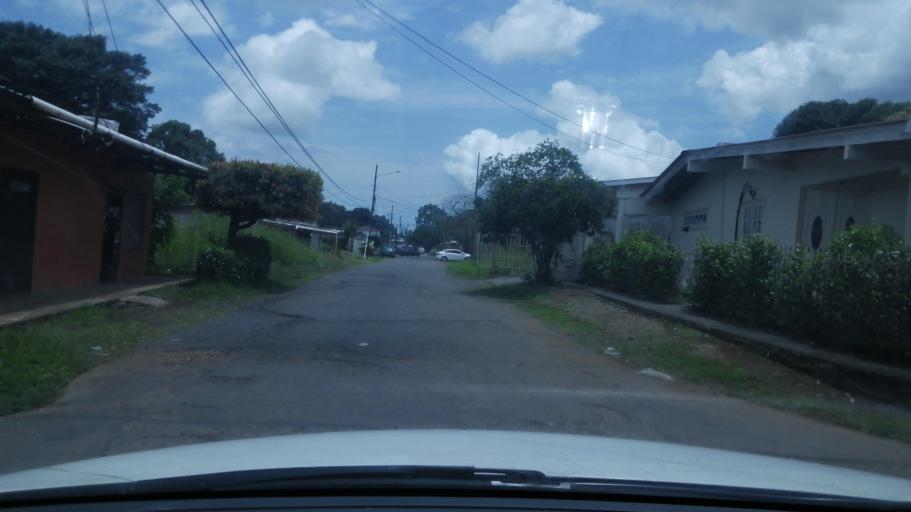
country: PA
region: Chiriqui
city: David
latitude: 8.4243
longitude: -82.4241
